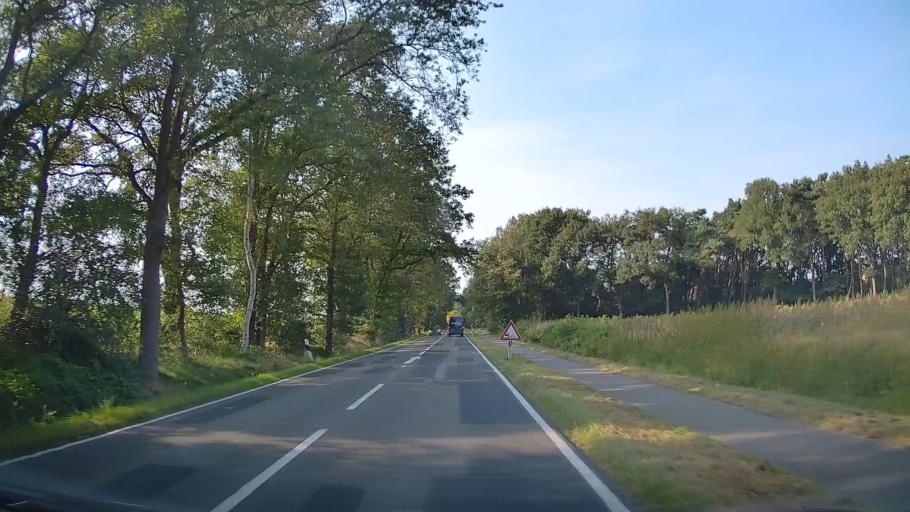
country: DE
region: Lower Saxony
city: Friesoythe
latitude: 53.1124
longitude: 7.8273
